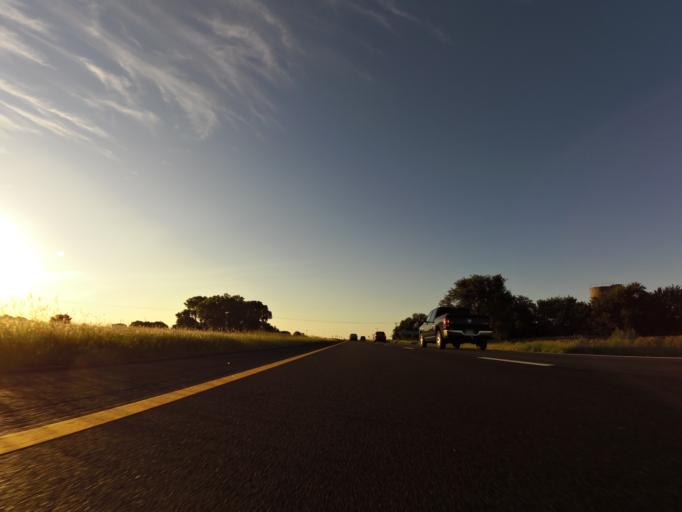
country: US
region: Kansas
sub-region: Sedgwick County
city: Colwich
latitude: 37.8567
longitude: -97.6119
